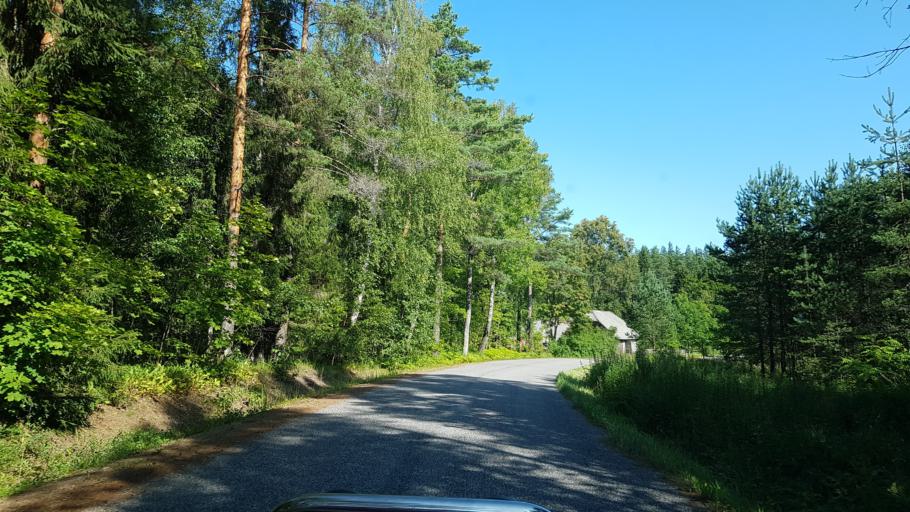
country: EE
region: Vorumaa
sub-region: Voru linn
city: Voru
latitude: 57.7144
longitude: 27.1956
